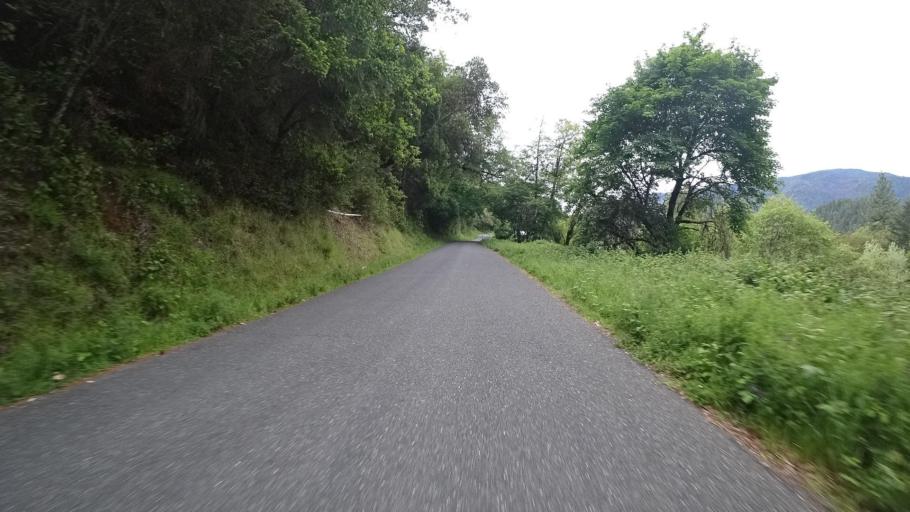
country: US
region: California
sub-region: Humboldt County
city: Willow Creek
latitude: 40.9456
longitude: -123.6110
